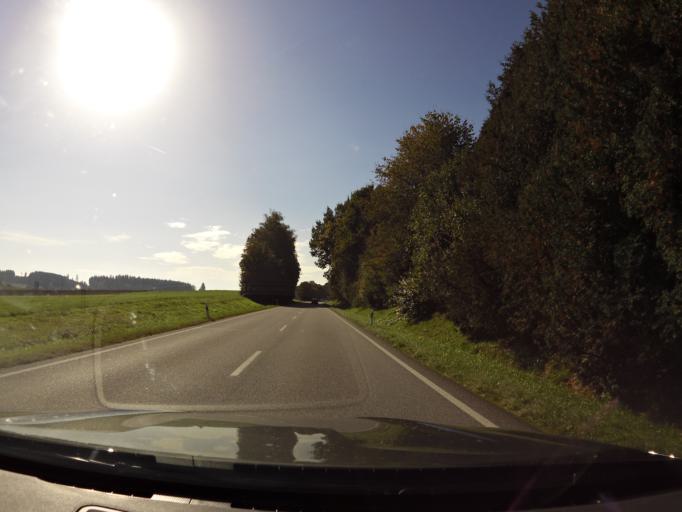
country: DE
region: Bavaria
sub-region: Lower Bavaria
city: Altfraunhofen
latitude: 48.4410
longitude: 12.1424
